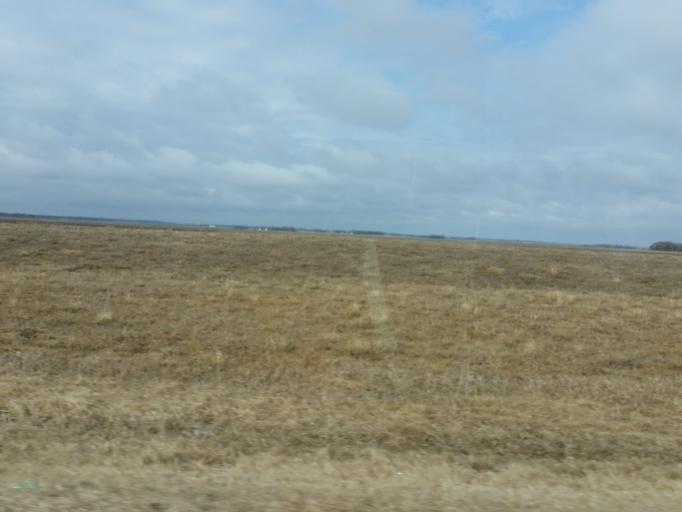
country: US
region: North Dakota
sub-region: Traill County
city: Mayville
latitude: 47.4637
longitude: -97.3261
